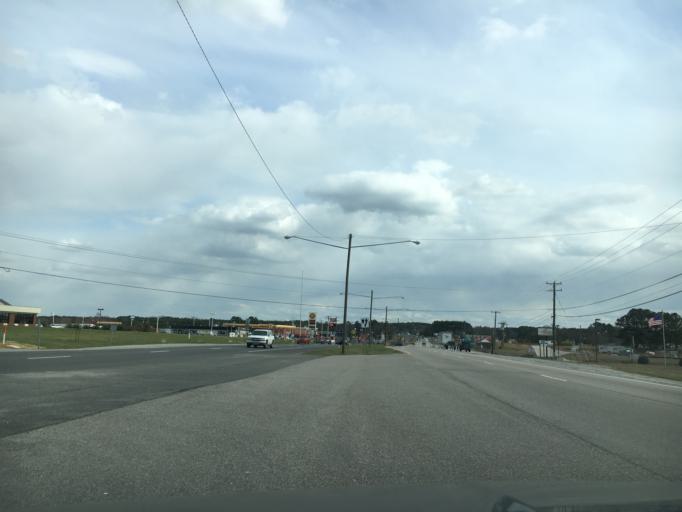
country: US
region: Virginia
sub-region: Mecklenburg County
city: South Hill
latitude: 36.7120
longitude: -78.1112
